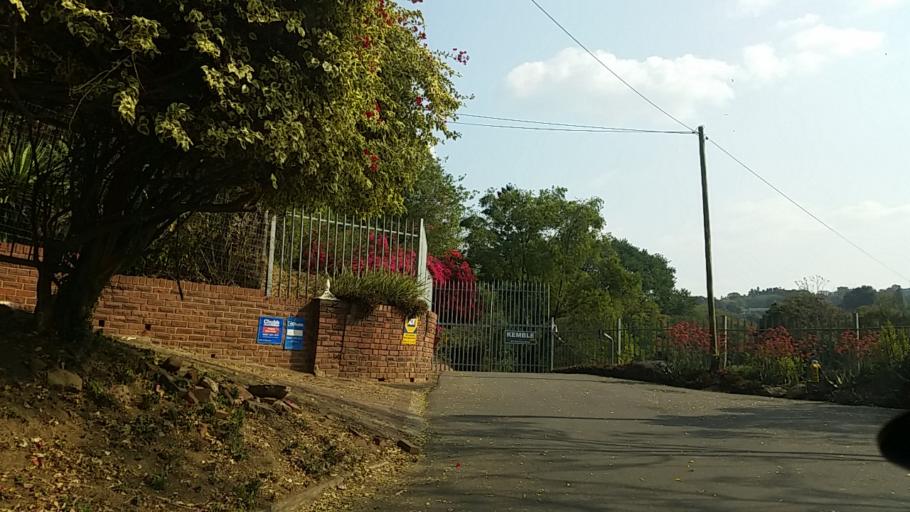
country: ZA
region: KwaZulu-Natal
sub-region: eThekwini Metropolitan Municipality
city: Berea
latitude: -29.8364
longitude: 30.9461
